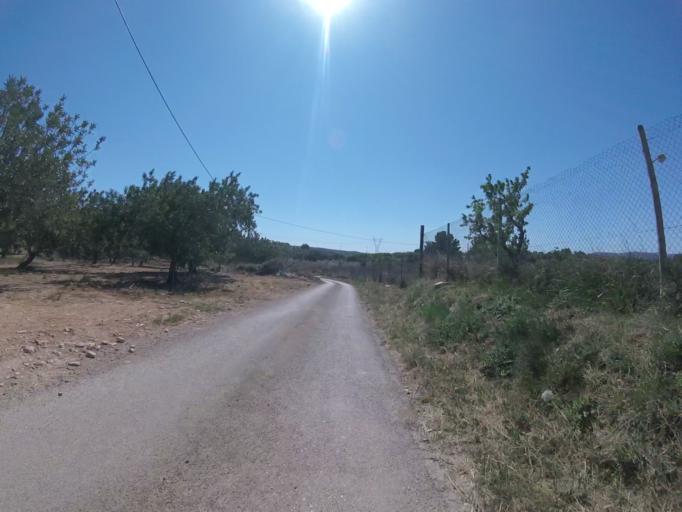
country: ES
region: Valencia
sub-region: Provincia de Castello
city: Cuevas de Vinroma
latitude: 40.3751
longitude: 0.1340
